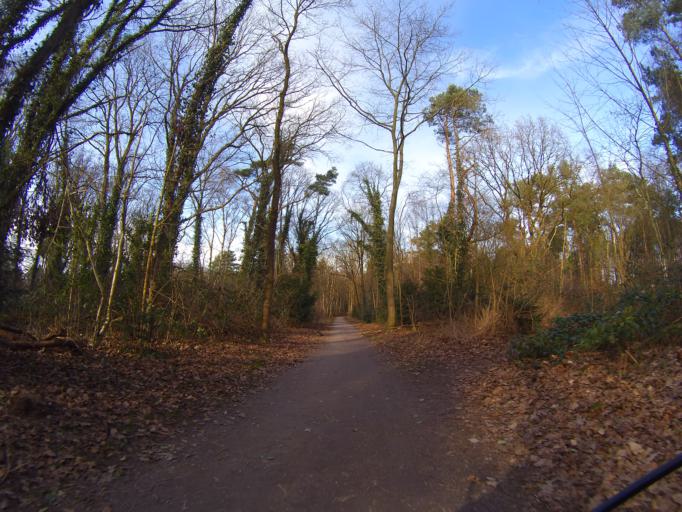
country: NL
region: North Holland
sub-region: Gemeente Hilversum
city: Hilversum
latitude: 52.2368
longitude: 5.1998
